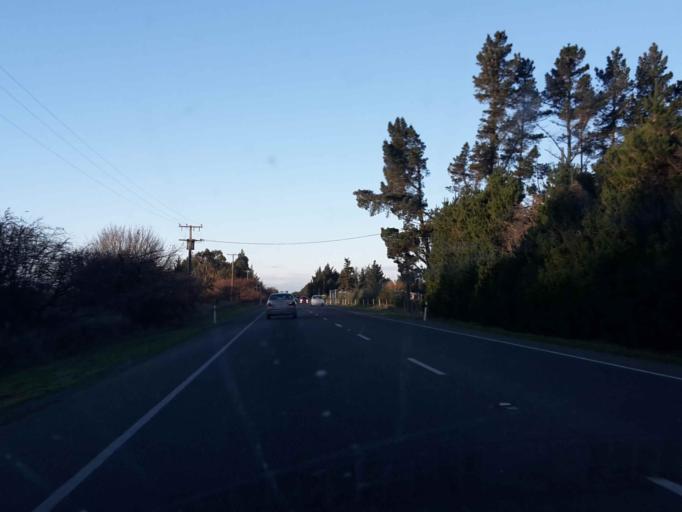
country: NZ
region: Canterbury
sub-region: Selwyn District
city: Burnham
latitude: -43.6139
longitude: 172.3182
